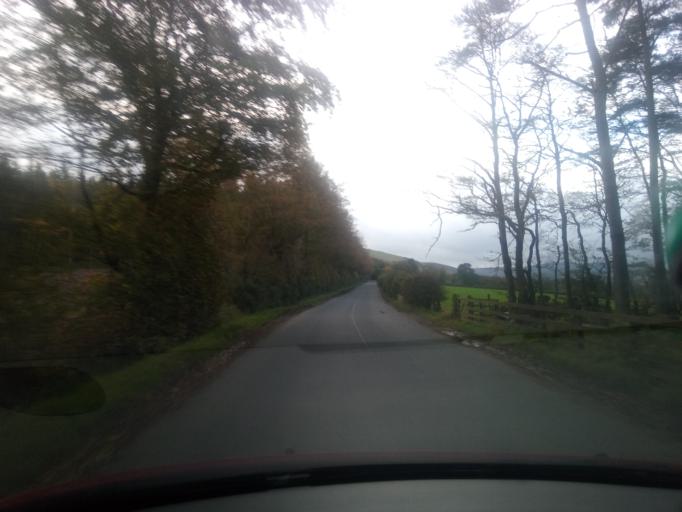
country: GB
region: Scotland
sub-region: The Scottish Borders
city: Jedburgh
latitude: 55.3879
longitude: -2.6434
